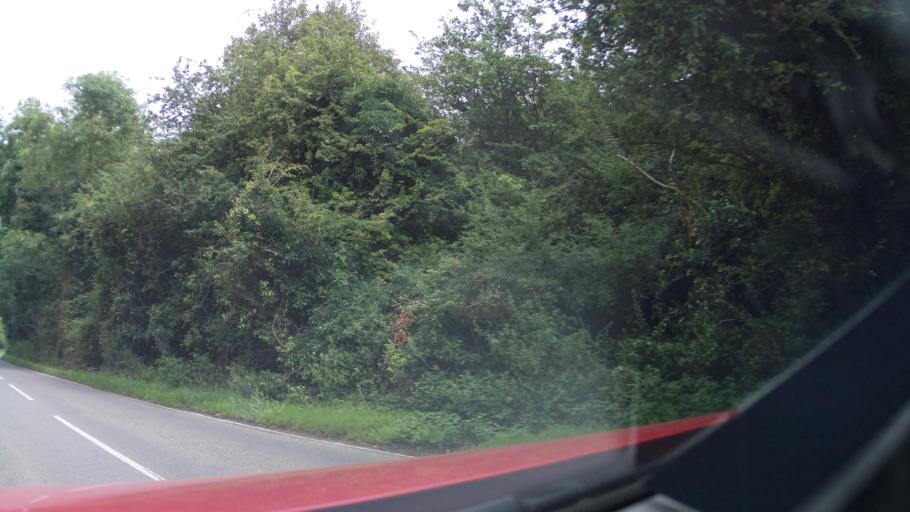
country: GB
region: England
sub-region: Northamptonshire
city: Corby
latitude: 52.5152
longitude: -0.6687
